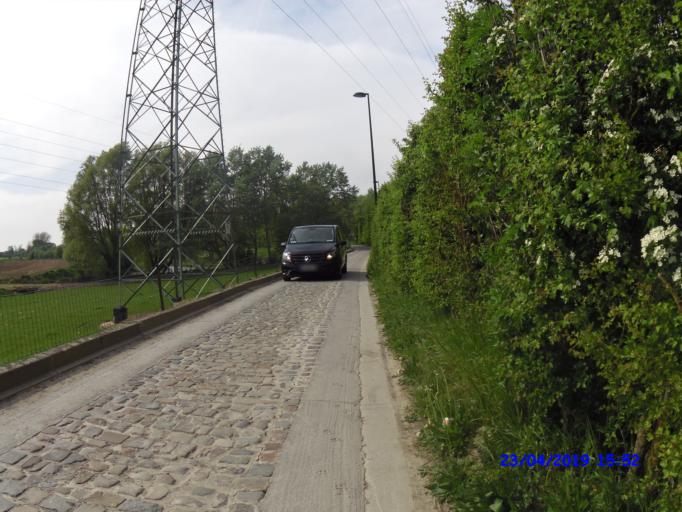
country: BE
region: Flanders
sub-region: Provincie Vlaams-Brabant
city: Dilbeek
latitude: 50.8122
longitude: 4.2743
